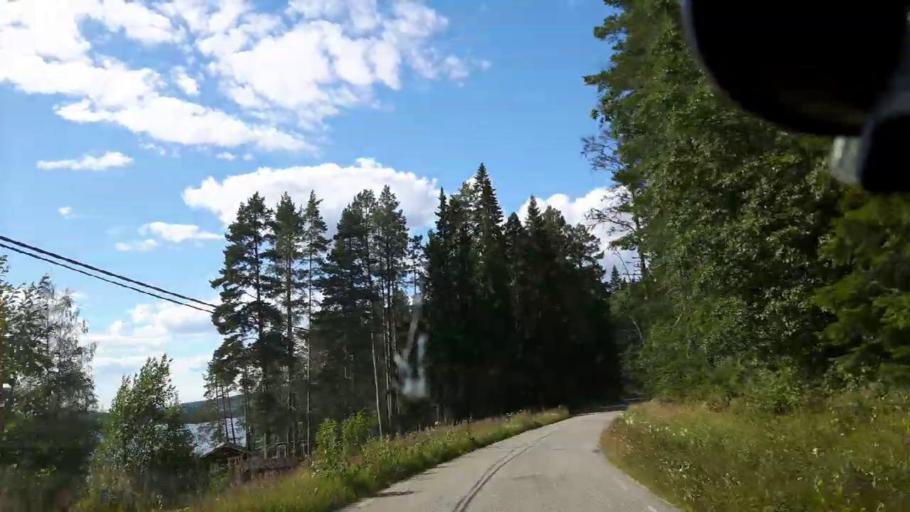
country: SE
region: Jaemtland
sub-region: Braecke Kommun
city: Braecke
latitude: 62.8628
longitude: 15.2743
